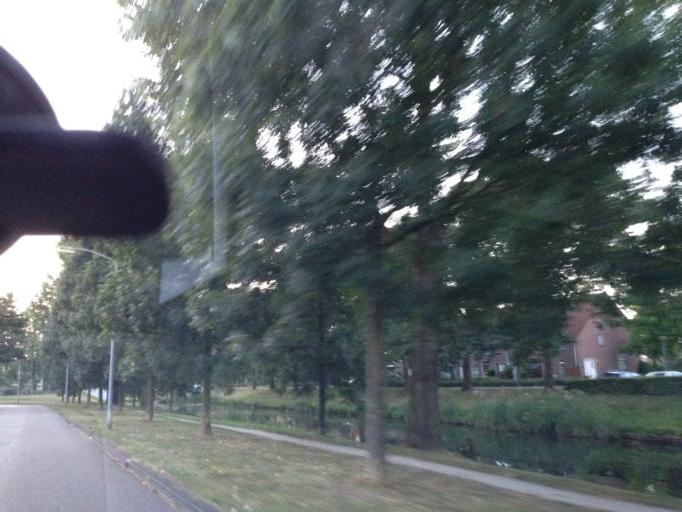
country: NL
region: Flevoland
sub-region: Gemeente Almere
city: Almere Stad
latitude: 52.3612
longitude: 5.2077
